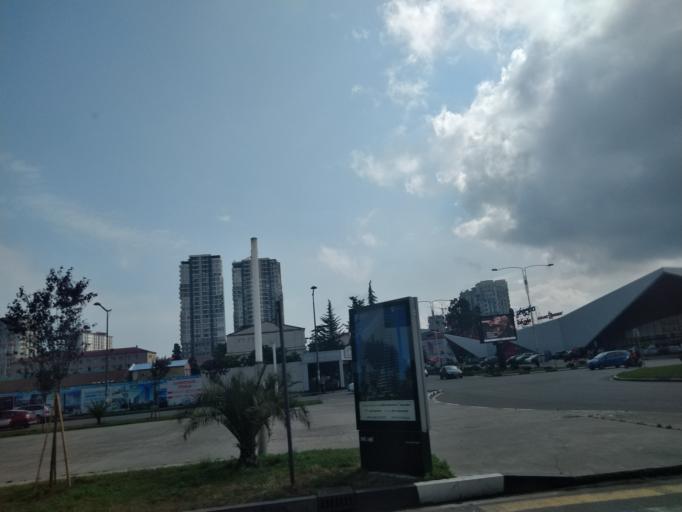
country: GE
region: Ajaria
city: Batumi
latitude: 41.6373
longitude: 41.6183
